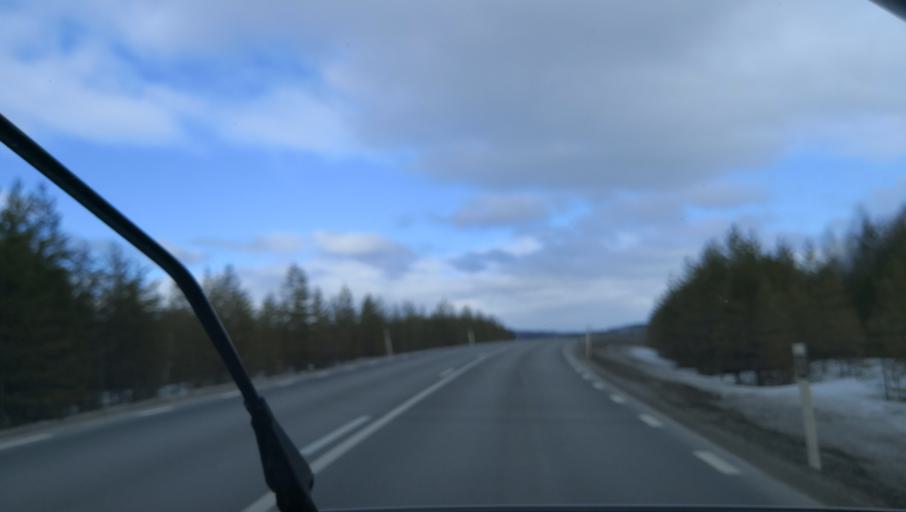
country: SE
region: Vaesterbotten
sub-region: Vannas Kommun
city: Vaennaes
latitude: 63.9218
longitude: 19.7421
